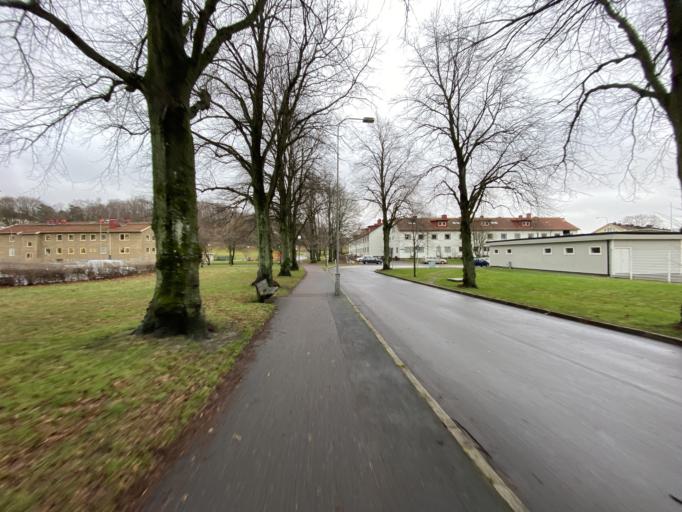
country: SE
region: Vaestra Goetaland
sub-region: Goteborg
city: Eriksbo
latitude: 57.7356
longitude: 12.0166
